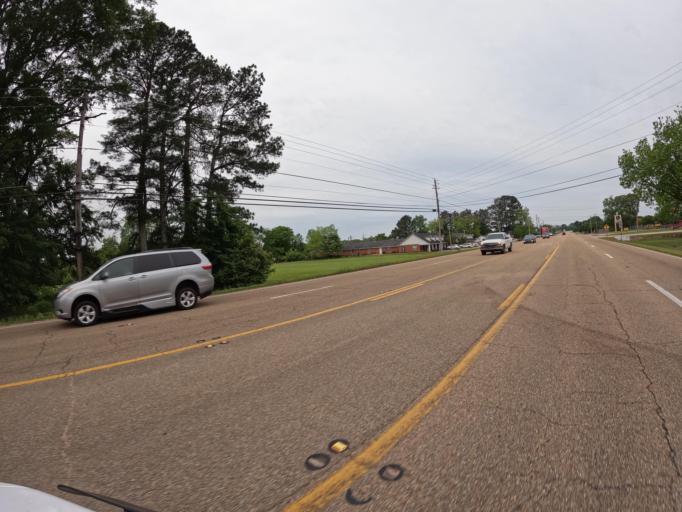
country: US
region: Mississippi
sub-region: Lee County
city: Tupelo
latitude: 34.2944
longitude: -88.7620
